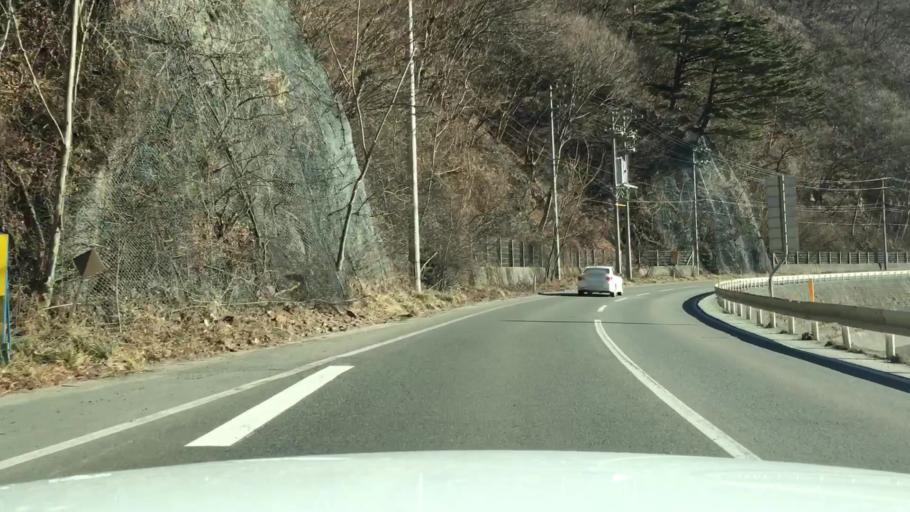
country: JP
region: Iwate
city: Miyako
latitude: 39.6188
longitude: 141.7924
